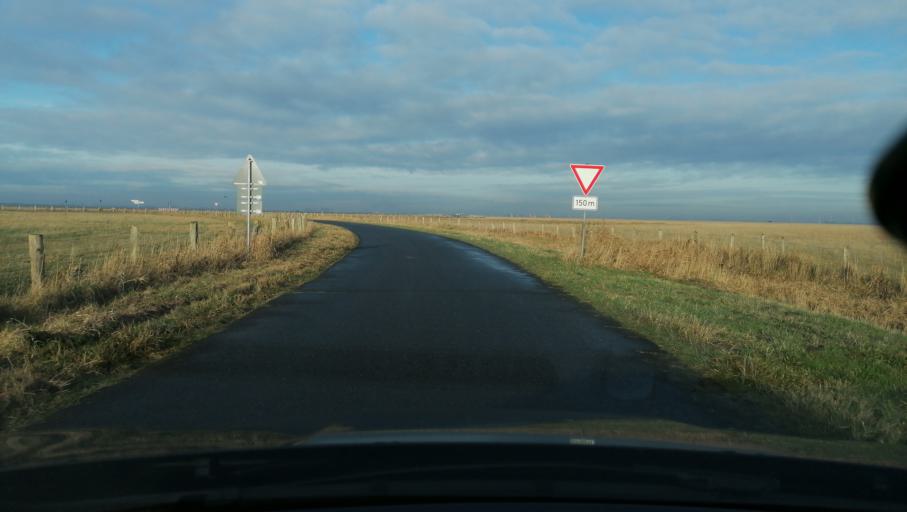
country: DE
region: Schleswig-Holstein
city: Friedrichsgabekoog
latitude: 54.1108
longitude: 8.9526
